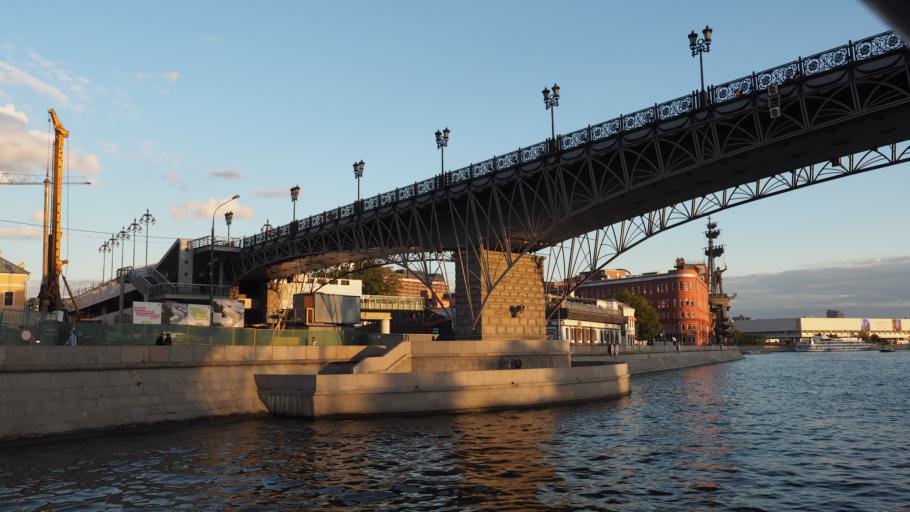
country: RU
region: Moscow
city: Moscow
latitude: 55.7438
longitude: 37.6090
